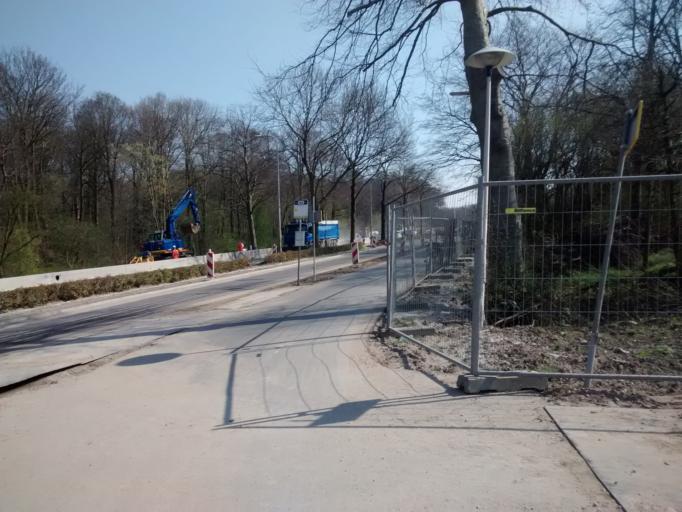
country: NL
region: Utrecht
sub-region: Gemeente Utrecht
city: Lunetten
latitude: 52.0722
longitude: 5.1480
